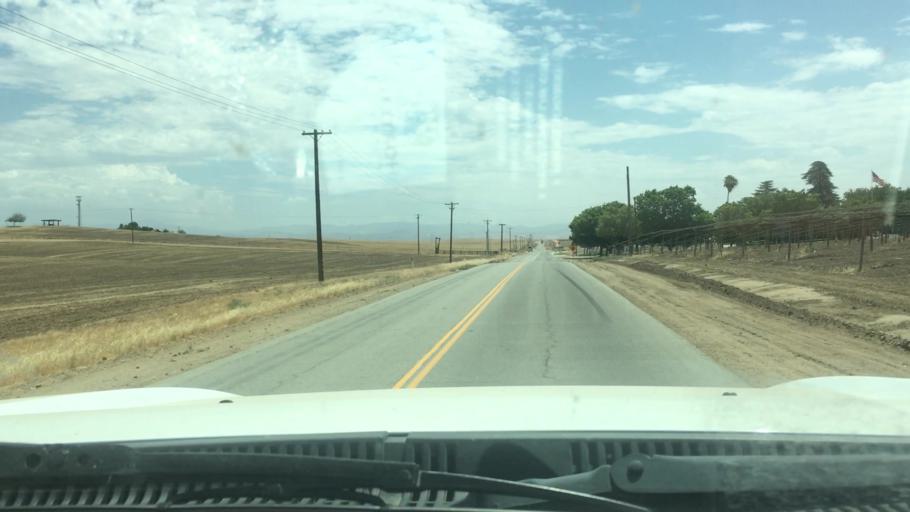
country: US
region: California
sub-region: Kern County
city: McFarland
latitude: 35.6025
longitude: -119.0928
